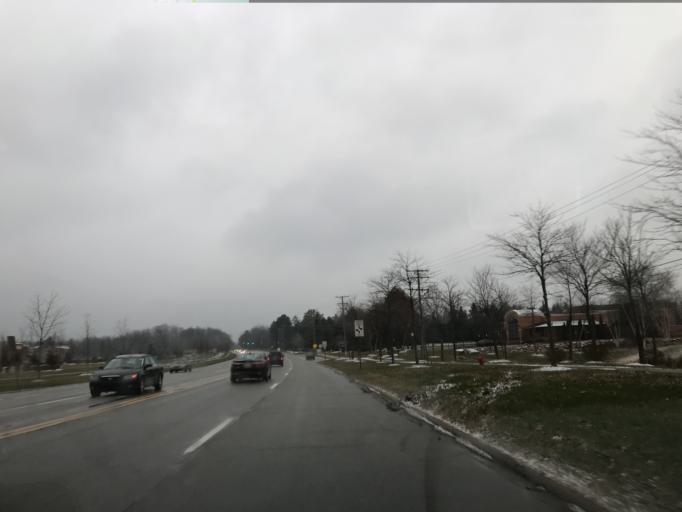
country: US
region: Michigan
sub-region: Wayne County
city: Northville
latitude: 42.4250
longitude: -83.4333
